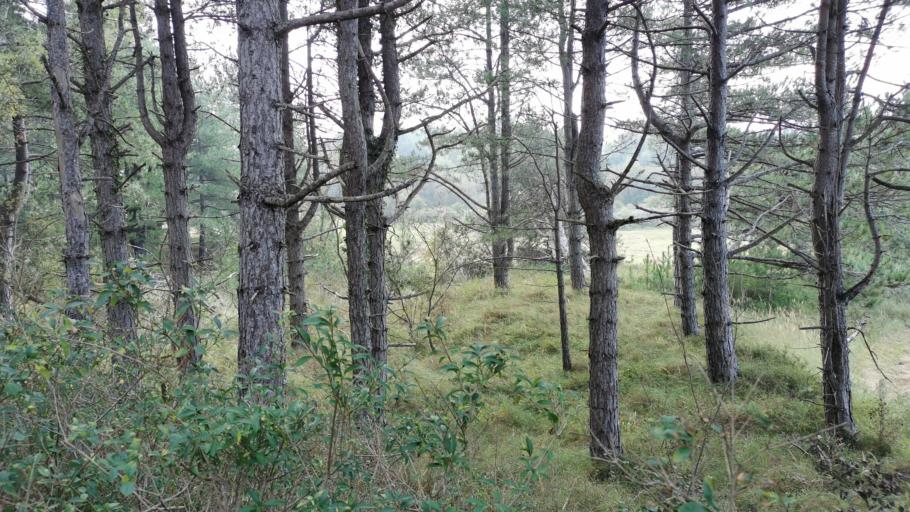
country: FR
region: Picardie
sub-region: Departement de la Somme
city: Fort-Mahon-Plage
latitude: 50.3315
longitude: 1.5595
